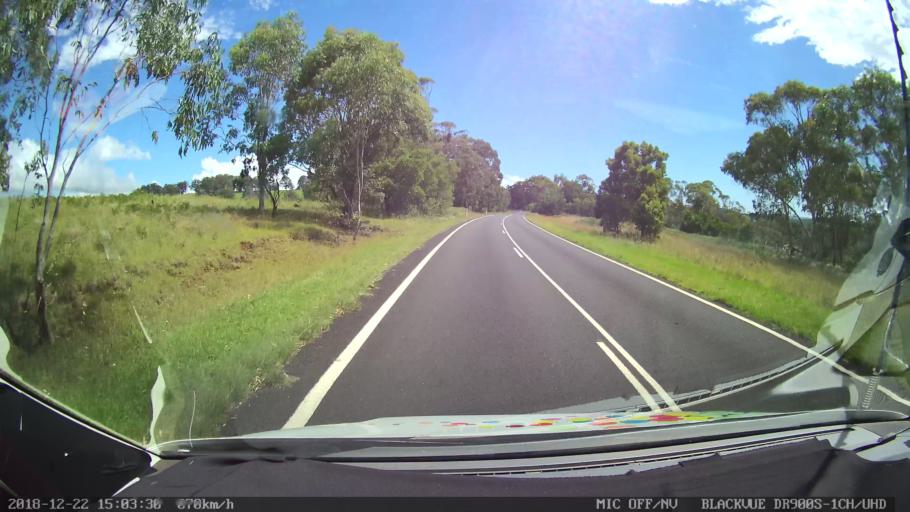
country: AU
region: New South Wales
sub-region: Bellingen
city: Dorrigo
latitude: -30.2651
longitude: 152.4406
